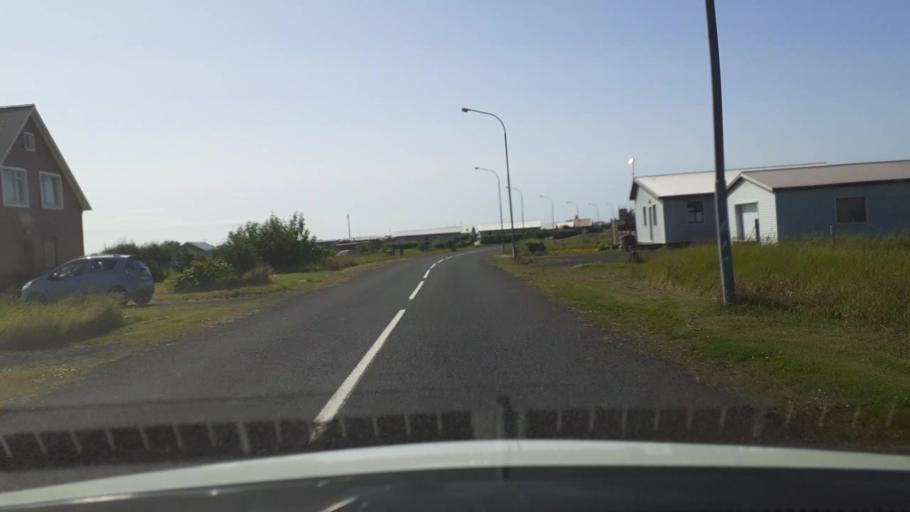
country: IS
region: South
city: Selfoss
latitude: 63.8402
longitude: -21.0544
